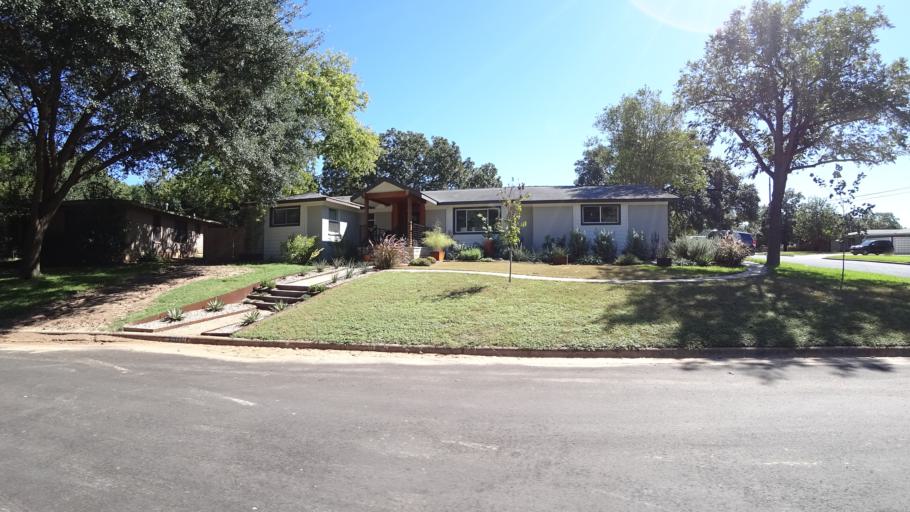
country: US
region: Texas
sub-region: Travis County
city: Rollingwood
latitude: 30.2291
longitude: -97.7945
